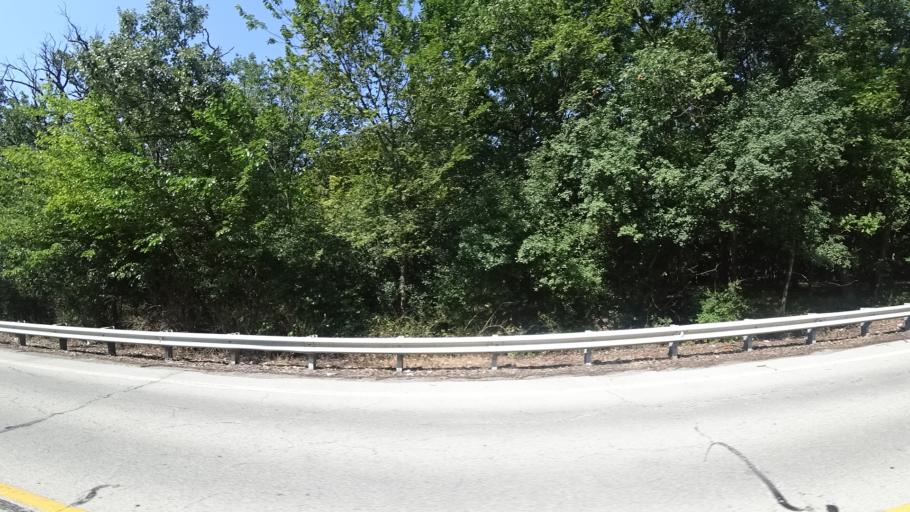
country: US
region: Illinois
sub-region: Cook County
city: Oak Forest
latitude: 41.5854
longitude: -87.7554
